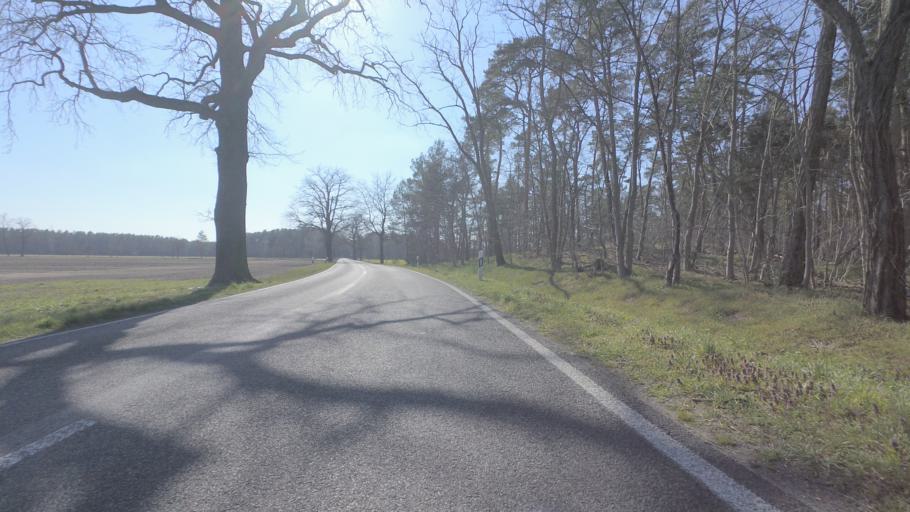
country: DE
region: Brandenburg
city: Munchehofe
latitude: 52.1248
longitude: 13.8022
